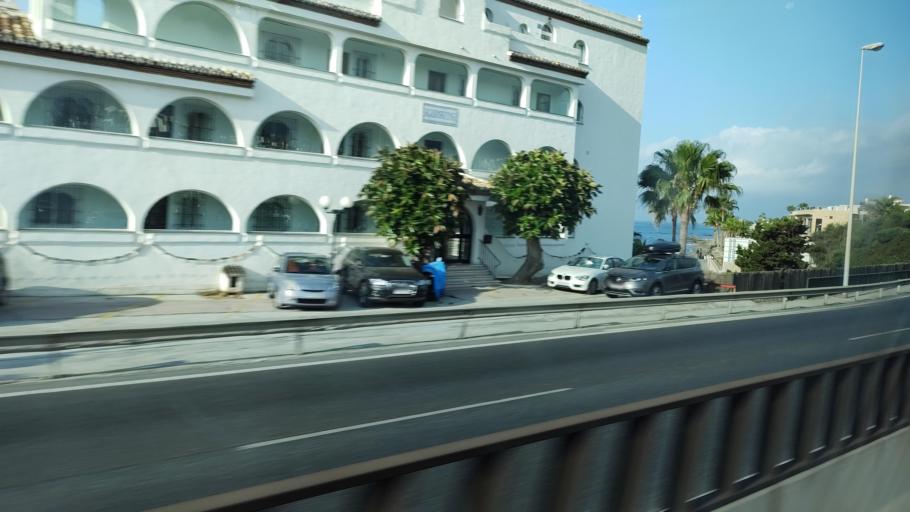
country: ES
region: Andalusia
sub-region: Provincia de Malaga
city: Fuengirola
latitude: 36.4911
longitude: -4.7042
